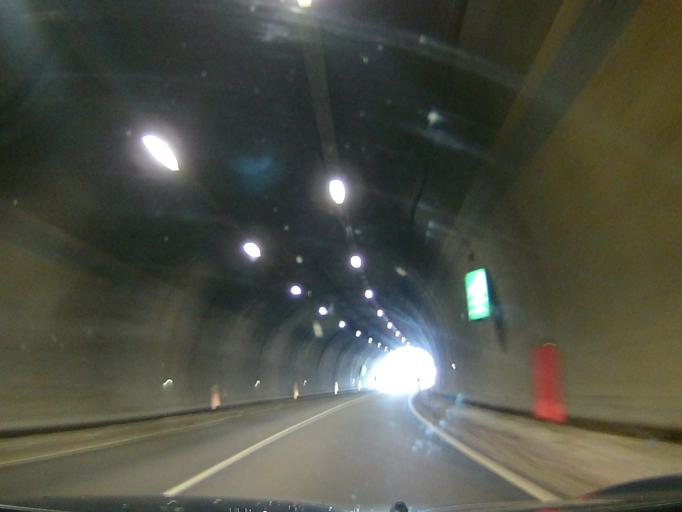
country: IT
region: Lombardy
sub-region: Provincia di Sondrio
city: Verceia
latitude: 46.1896
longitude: 9.4468
